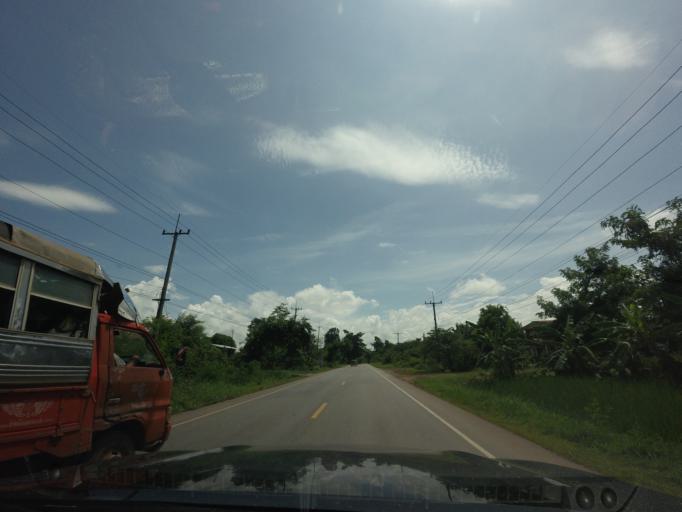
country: TH
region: Changwat Udon Thani
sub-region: Amphoe Ban Phue
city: Ban Phue
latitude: 17.7059
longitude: 102.4284
